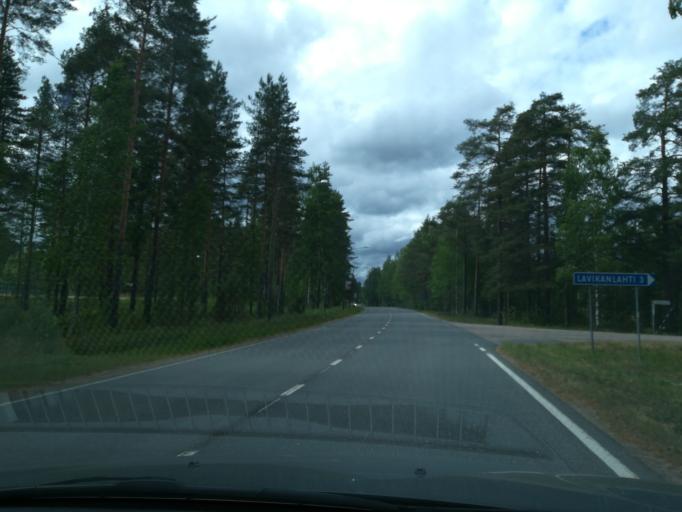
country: FI
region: South Karelia
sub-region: Lappeenranta
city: Savitaipale
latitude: 61.1937
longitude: 27.7064
